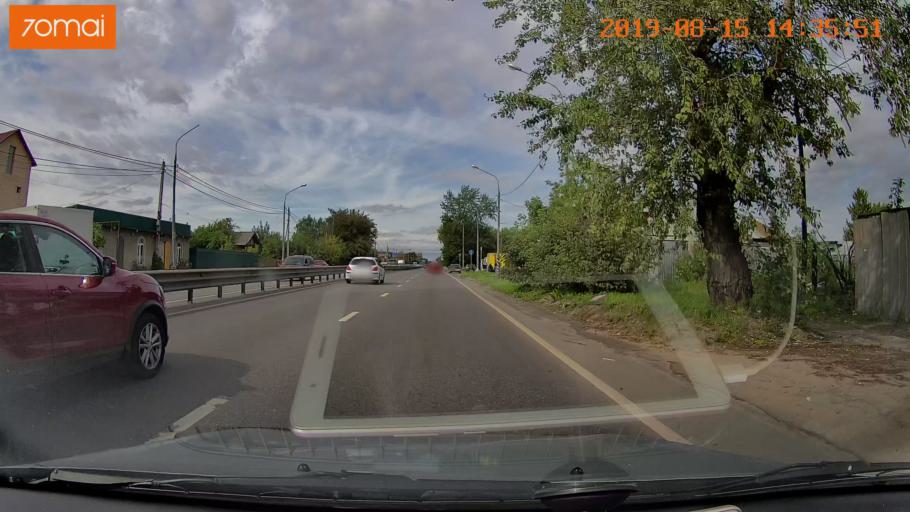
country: RU
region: Moskovskaya
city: Tomilino
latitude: 55.6416
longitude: 37.9367
